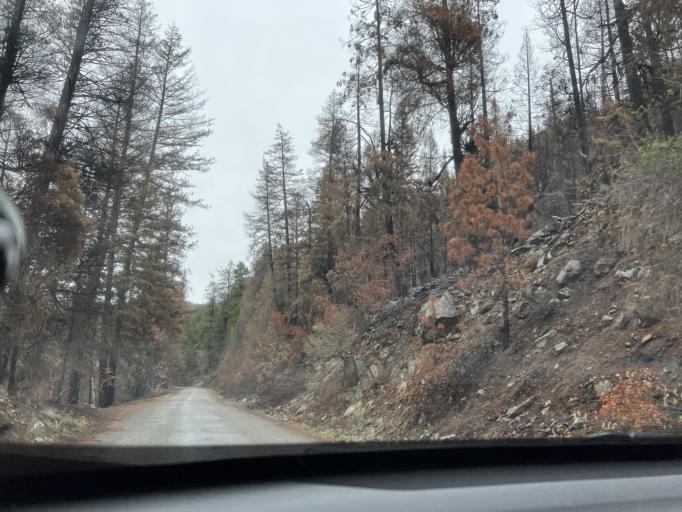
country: US
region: Washington
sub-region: Okanogan County
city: Brewster
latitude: 48.5680
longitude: -120.1732
